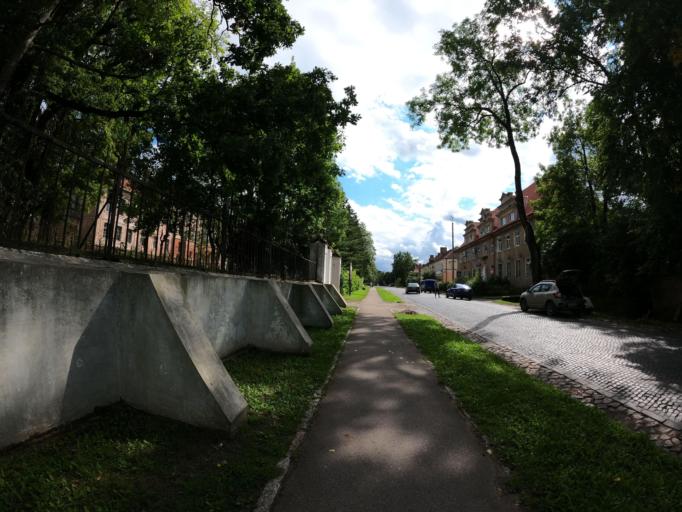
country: RU
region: Kaliningrad
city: Zheleznodorozhnyy
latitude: 54.3546
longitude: 21.3085
